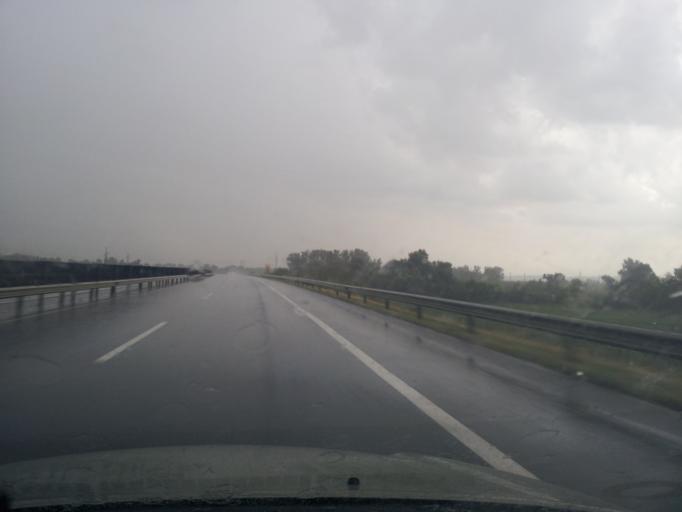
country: HU
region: Borsod-Abauj-Zemplen
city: Felsozsolca
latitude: 48.0994
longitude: 20.8463
